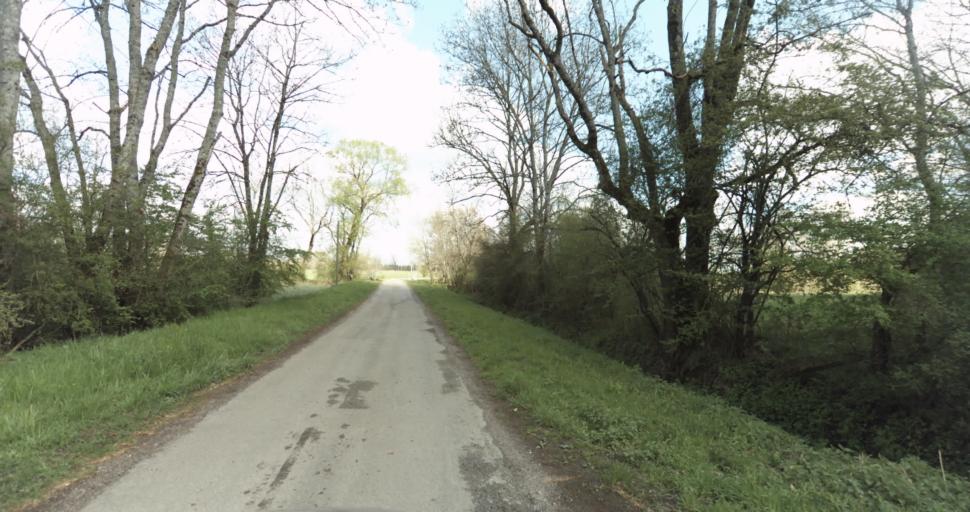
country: FR
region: Bourgogne
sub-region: Departement de la Cote-d'Or
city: Auxonne
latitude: 47.2004
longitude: 5.3918
